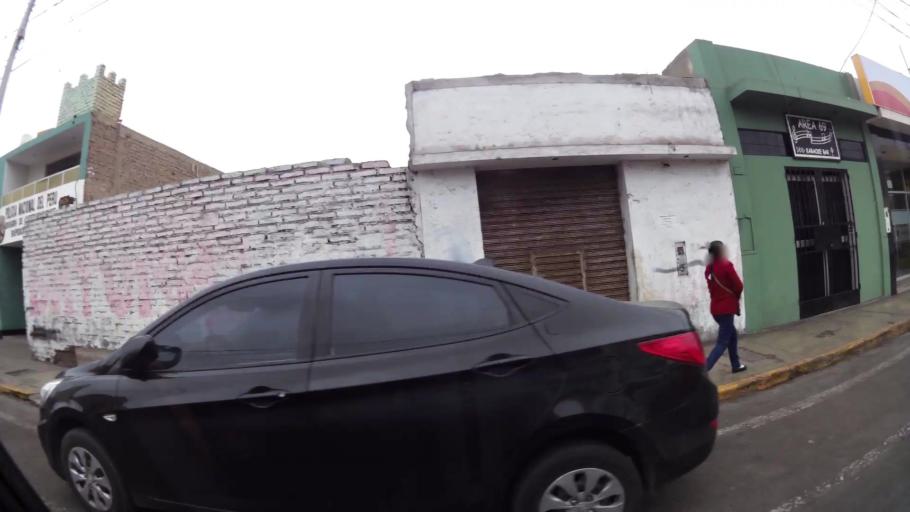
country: PE
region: Lima
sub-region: Barranca
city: Barranca
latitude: -10.7538
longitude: -77.7589
